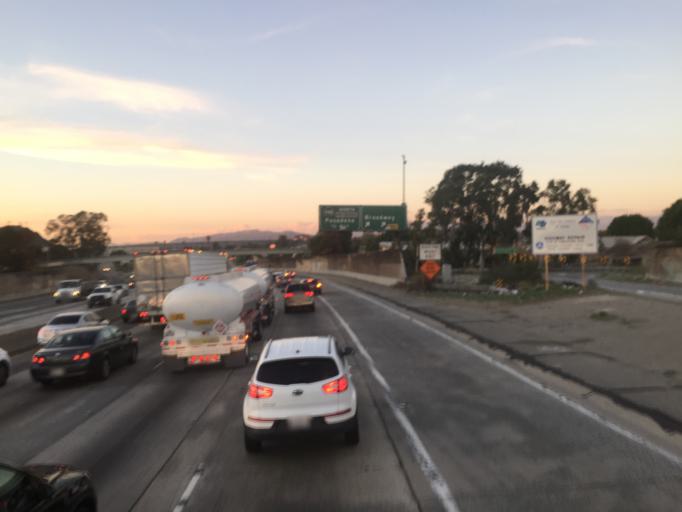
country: US
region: California
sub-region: Los Angeles County
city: Los Angeles
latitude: 34.0676
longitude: -118.2163
